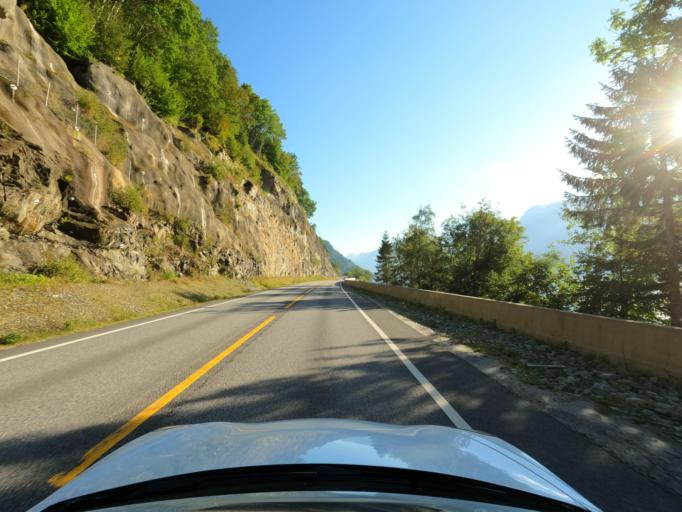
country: NO
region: Hordaland
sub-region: Ullensvang
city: Kinsarvik
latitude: 60.3089
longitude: 6.6476
